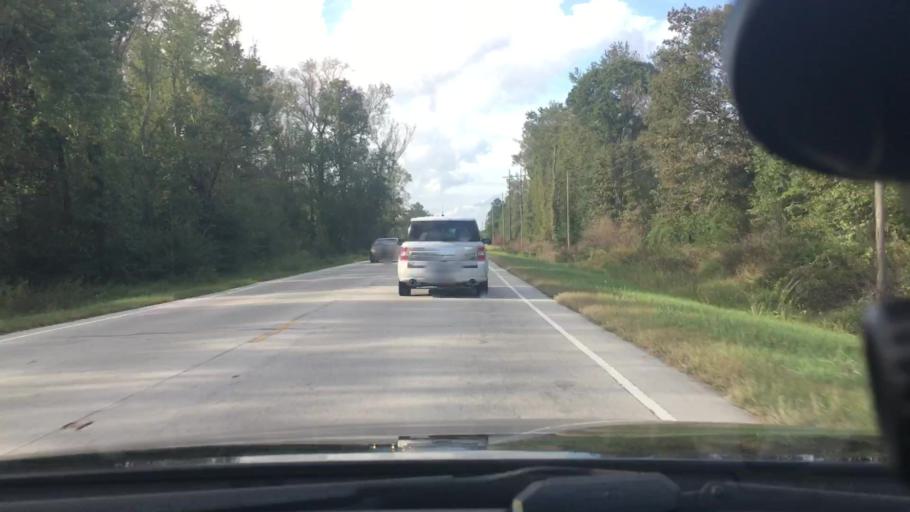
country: US
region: North Carolina
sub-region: Pitt County
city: Windsor
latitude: 35.4900
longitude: -77.3058
